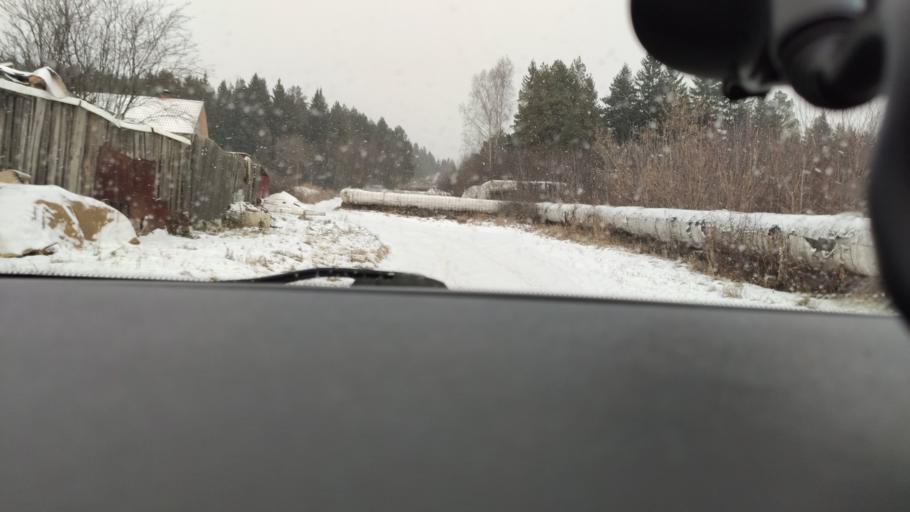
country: RU
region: Perm
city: Kondratovo
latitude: 57.9428
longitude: 56.1683
